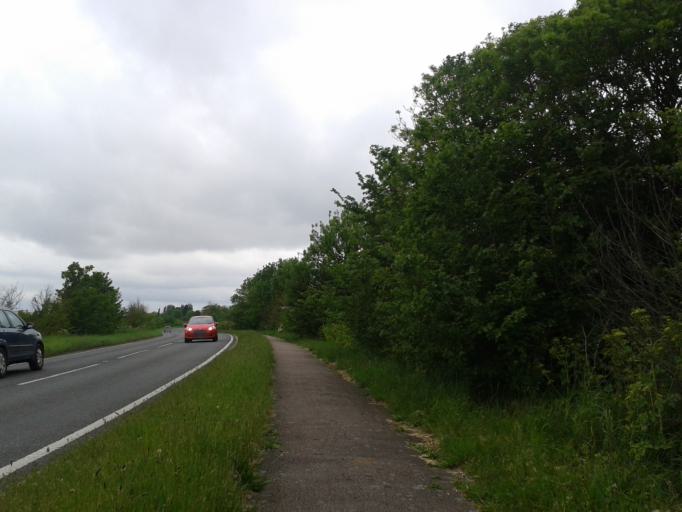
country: GB
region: England
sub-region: Cambridgeshire
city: Great Stukeley
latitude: 52.3470
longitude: -0.2004
